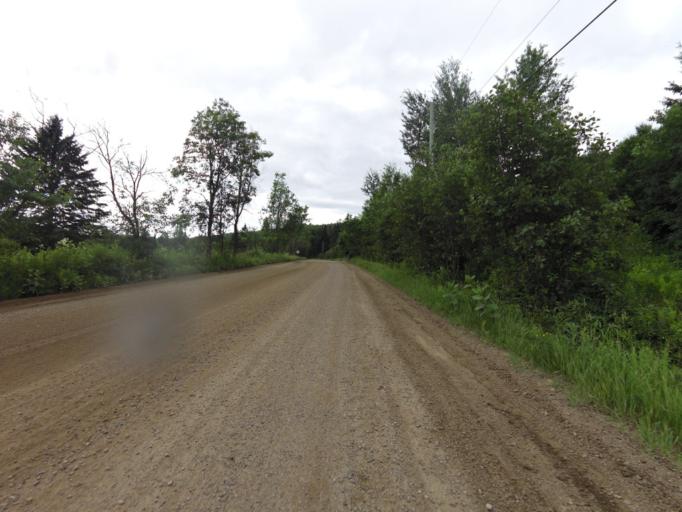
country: CA
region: Quebec
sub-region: Laurentides
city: Mont-Tremblant
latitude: 45.9408
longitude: -74.5979
